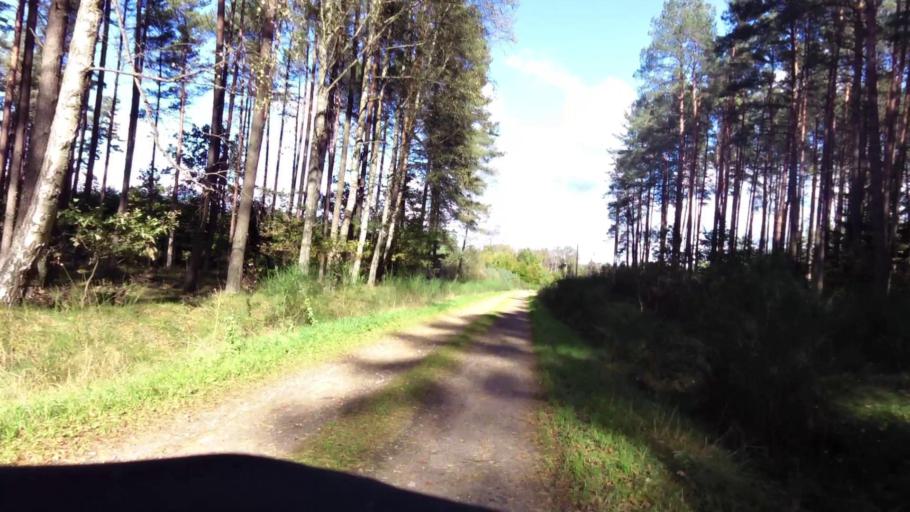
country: PL
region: West Pomeranian Voivodeship
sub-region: Powiat bialogardzki
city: Tychowo
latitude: 54.0295
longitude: 16.1529
